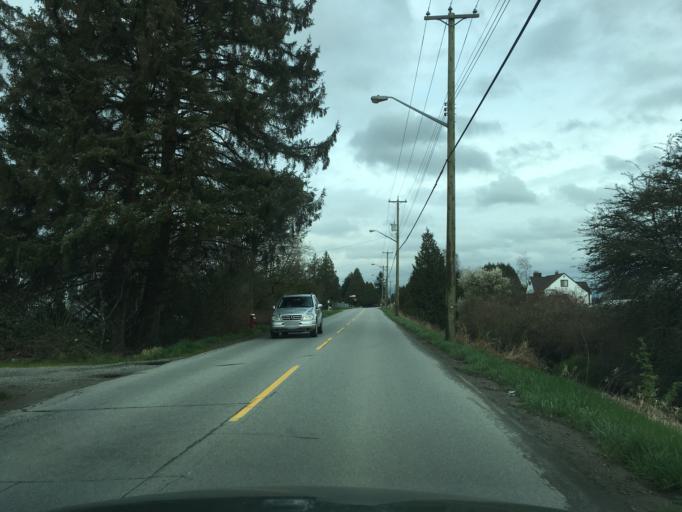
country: CA
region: British Columbia
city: Ladner
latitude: 49.1391
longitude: -123.0692
